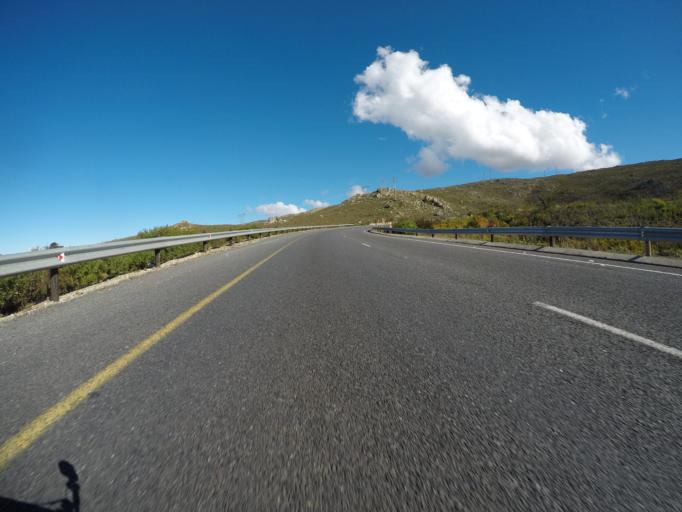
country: ZA
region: Western Cape
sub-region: Overberg District Municipality
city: Grabouw
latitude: -34.2234
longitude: 19.1745
